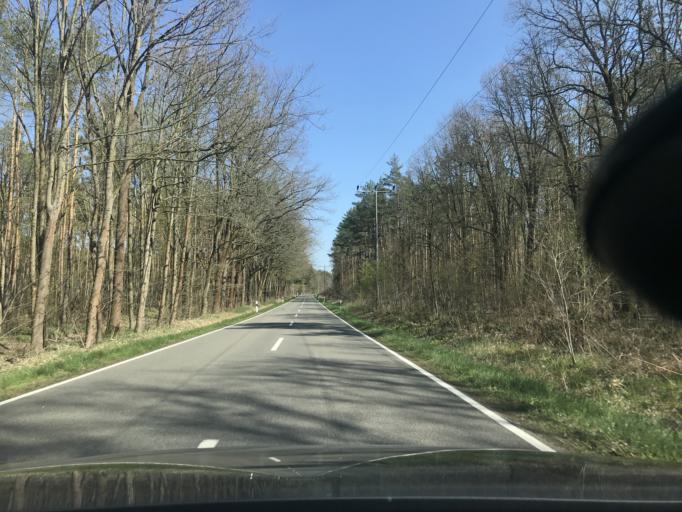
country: DE
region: Saxony
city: Bad Duben
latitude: 51.6348
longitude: 12.6096
